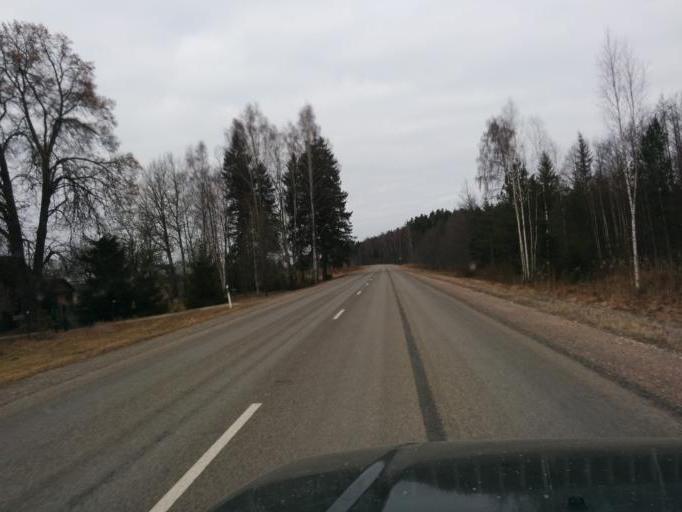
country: LV
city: Tireli
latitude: 56.8281
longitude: 23.6045
